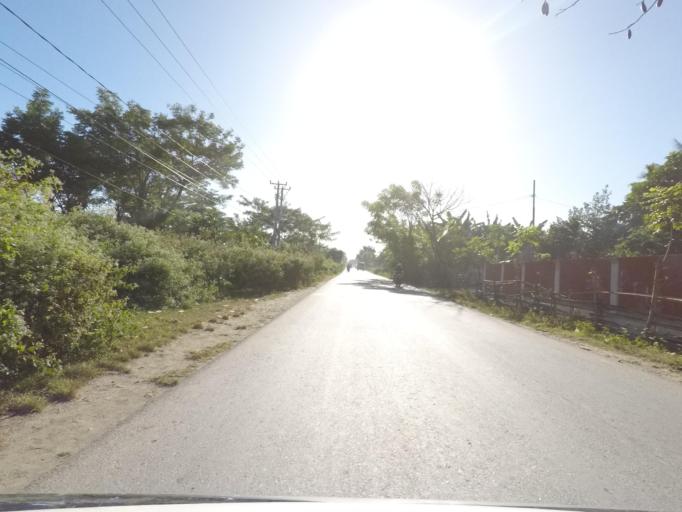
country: TL
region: Dili
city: Dili
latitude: -8.5539
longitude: 125.6580
